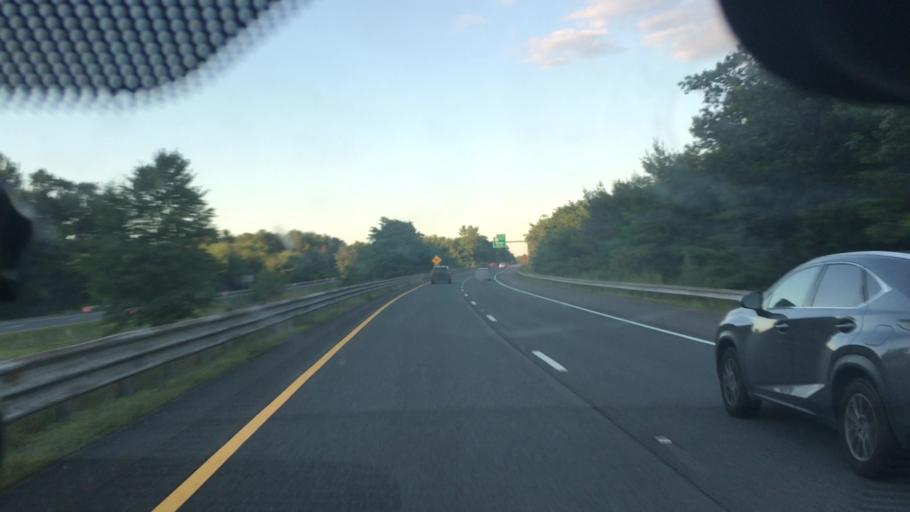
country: US
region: Massachusetts
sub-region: Franklin County
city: Greenfield
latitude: 42.6093
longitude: -72.6086
